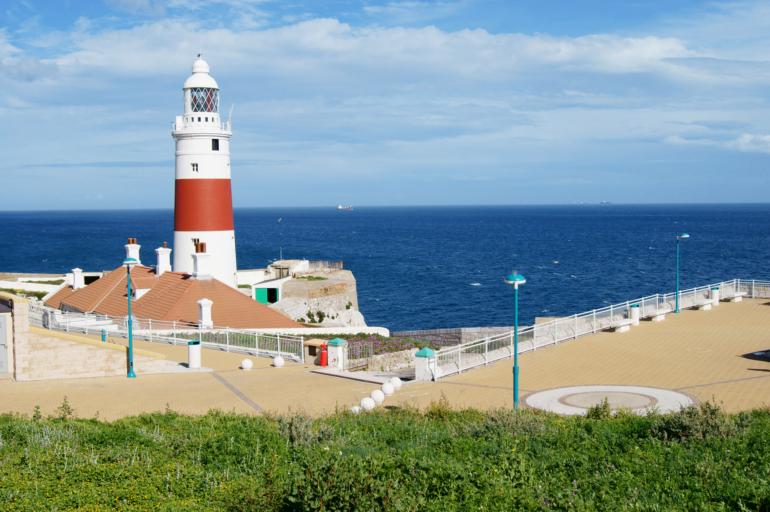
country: GI
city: Gibraltar
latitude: 36.1096
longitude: -5.3459
